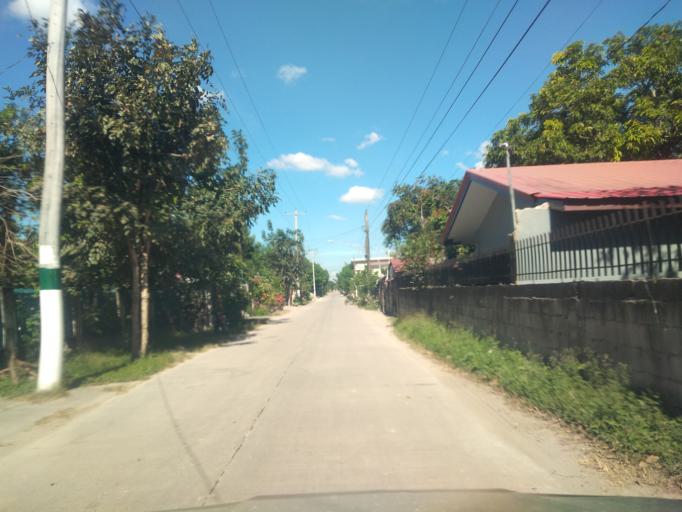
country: PH
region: Central Luzon
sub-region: Province of Pampanga
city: Bacolor
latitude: 15.0077
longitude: 120.6396
